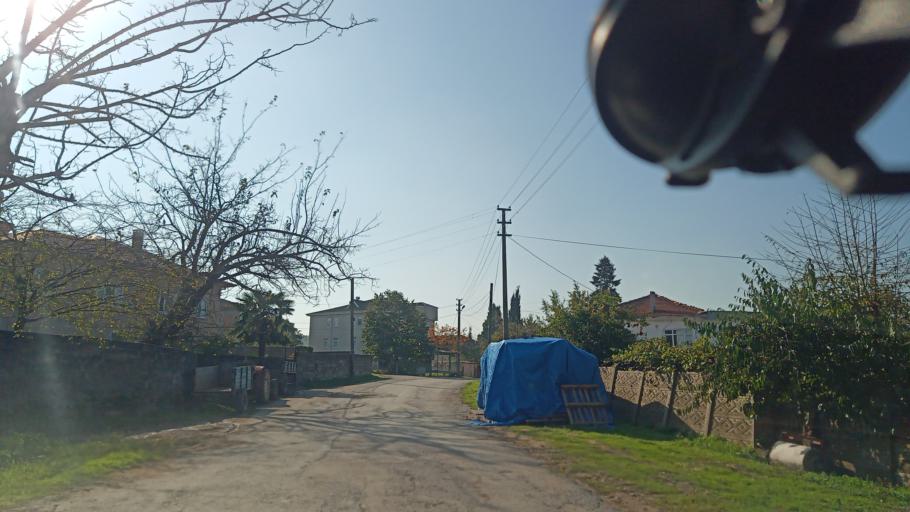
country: TR
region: Sakarya
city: Karasu
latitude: 41.0605
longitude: 30.7946
